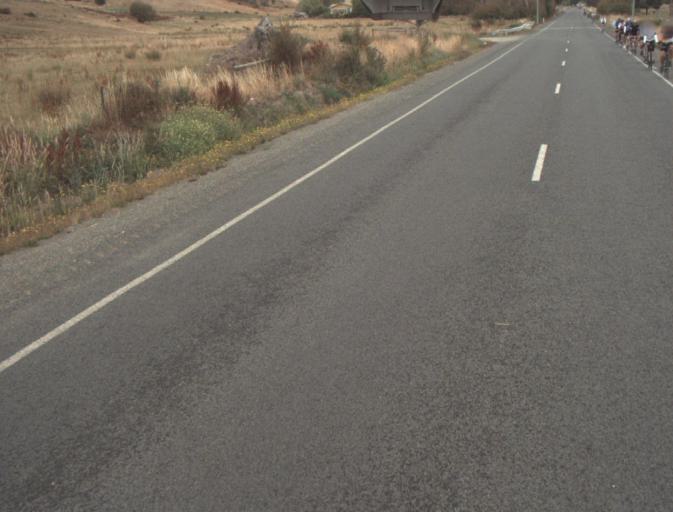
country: AU
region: Tasmania
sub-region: Launceston
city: Mayfield
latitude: -41.2409
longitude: 147.2161
